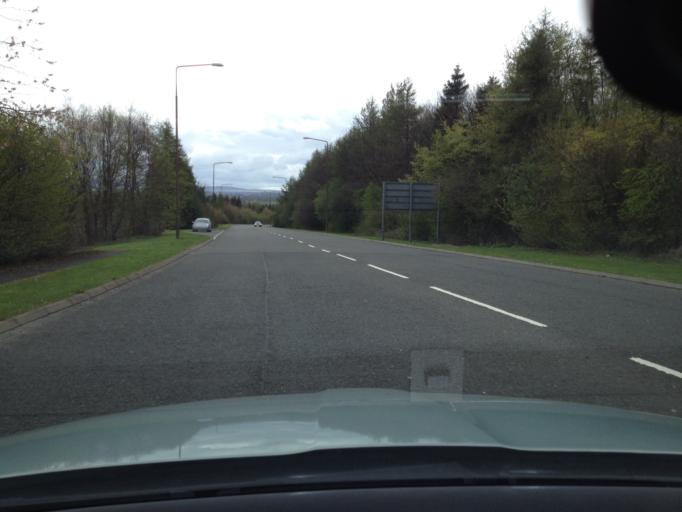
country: GB
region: Scotland
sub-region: West Lothian
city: Livingston
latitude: 55.8947
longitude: -3.5607
